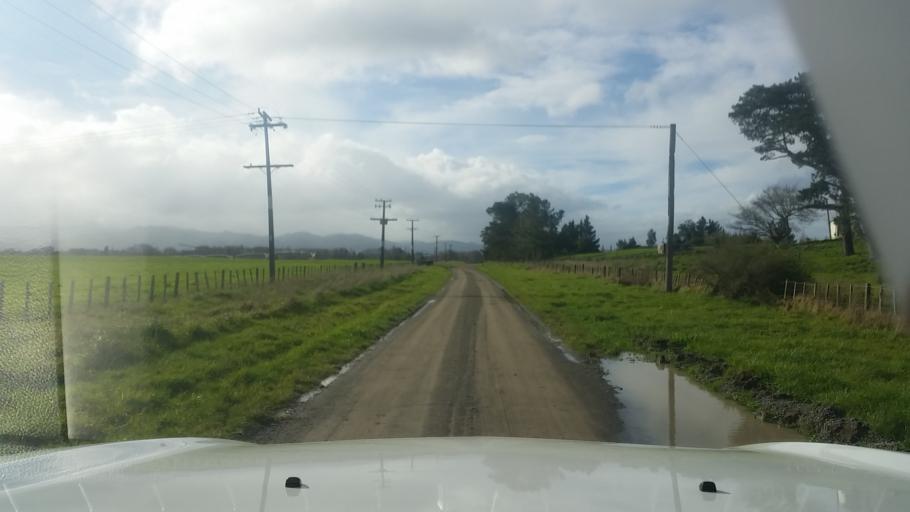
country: NZ
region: Wellington
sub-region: Masterton District
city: Masterton
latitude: -41.1035
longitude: 175.4709
